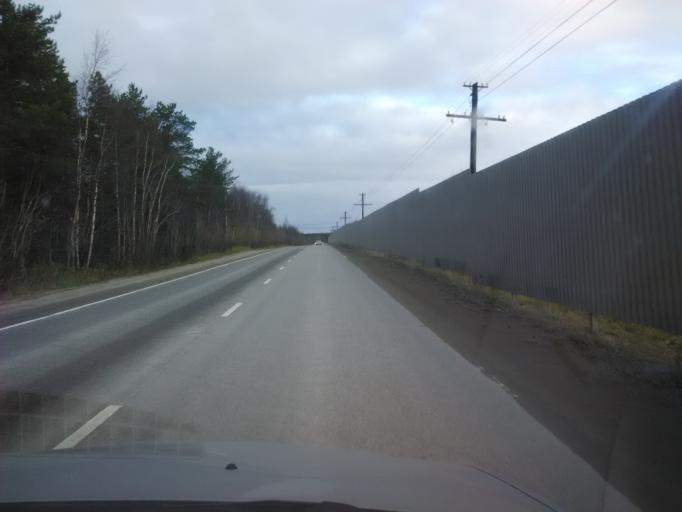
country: RU
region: Murmansk
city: Polyarnyye Zori
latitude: 67.3829
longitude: 32.5116
